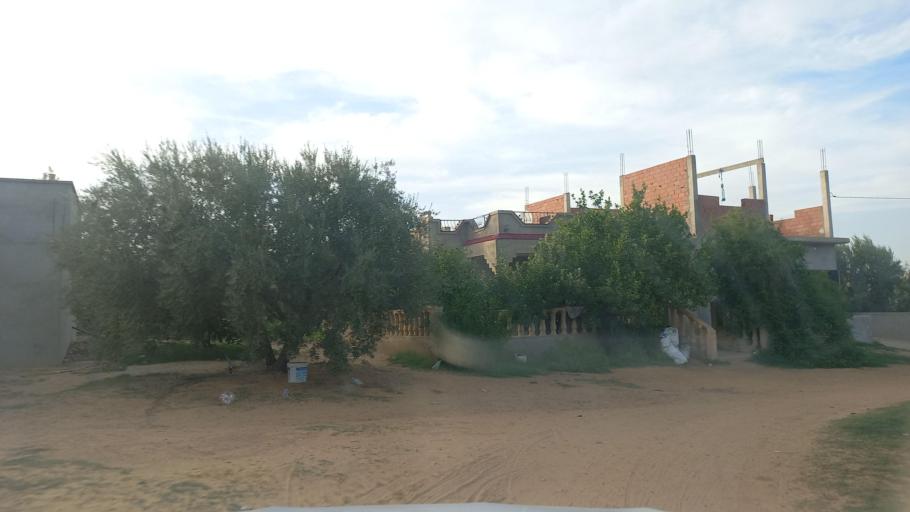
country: TN
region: Al Qasrayn
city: Kasserine
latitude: 35.2514
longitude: 9.0391
